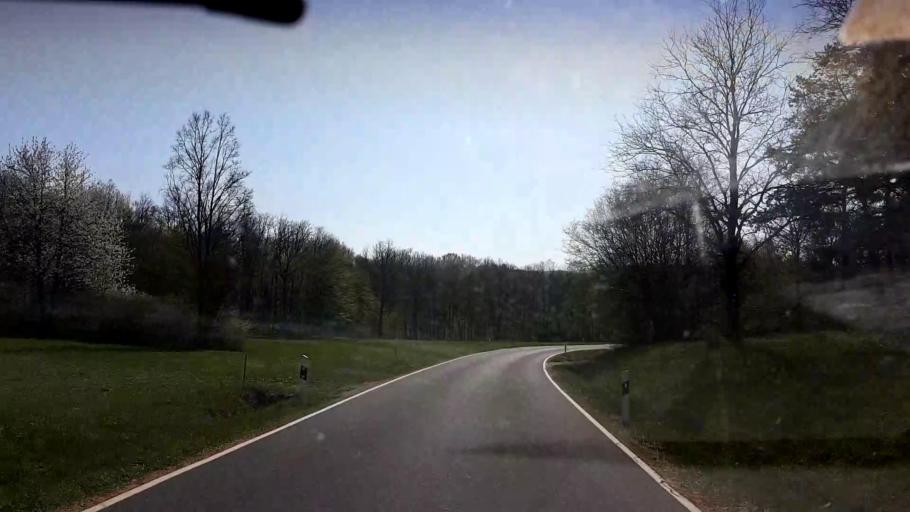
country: DE
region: Bavaria
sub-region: Upper Franconia
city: Pottenstein
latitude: 49.7940
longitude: 11.3948
